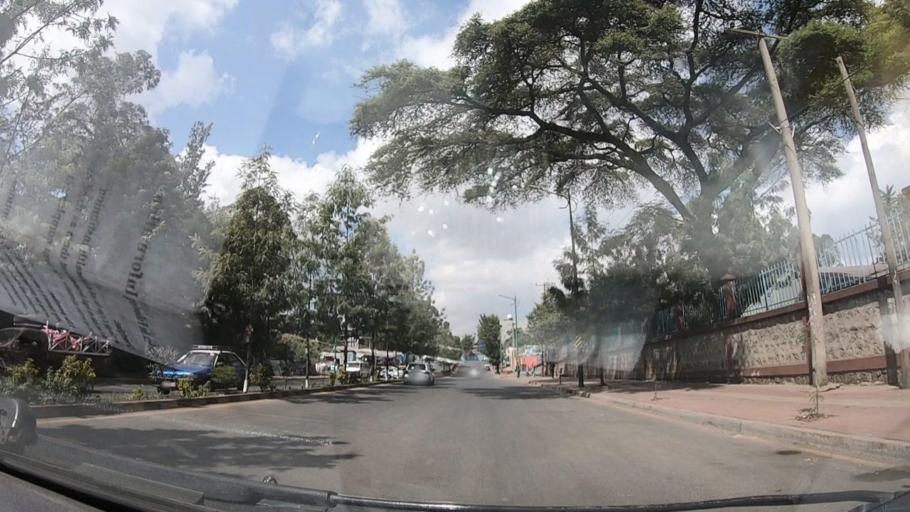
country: ET
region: Adis Abeba
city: Addis Ababa
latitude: 9.0029
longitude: 38.7353
